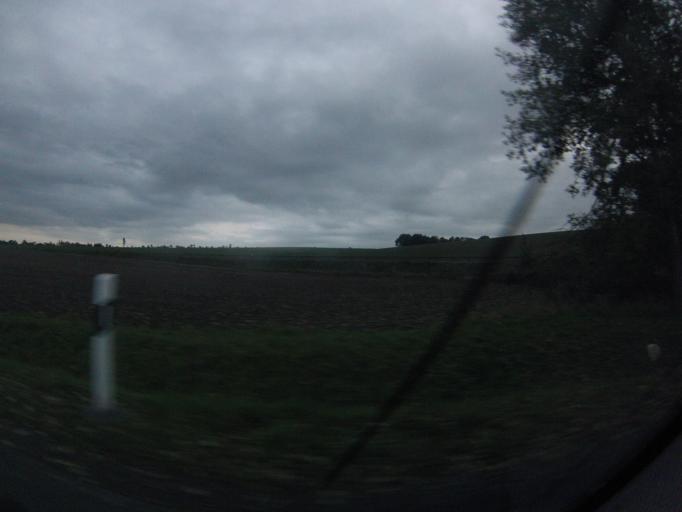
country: DE
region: Thuringia
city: Saara
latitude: 50.9268
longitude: 12.4115
